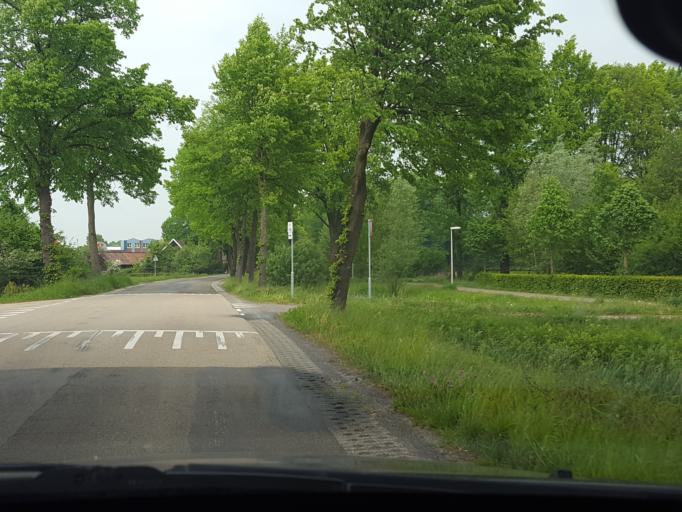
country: NL
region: Gelderland
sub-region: Gemeente Winterswijk
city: Winterswijk
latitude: 51.9619
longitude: 6.7375
